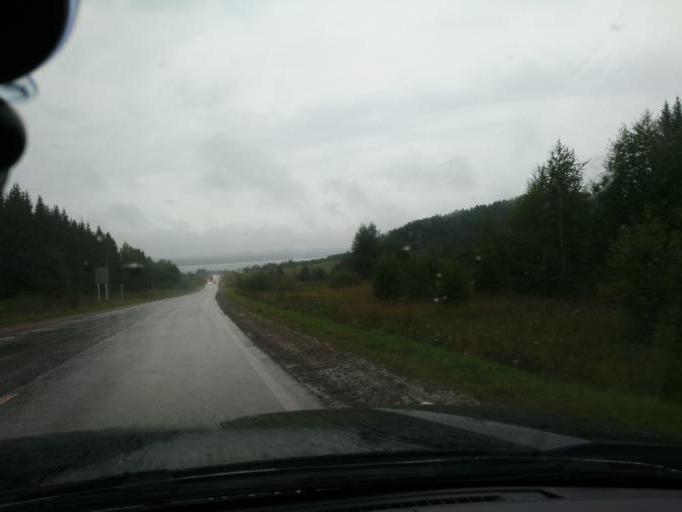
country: RU
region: Perm
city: Osa
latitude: 57.3261
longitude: 55.6007
